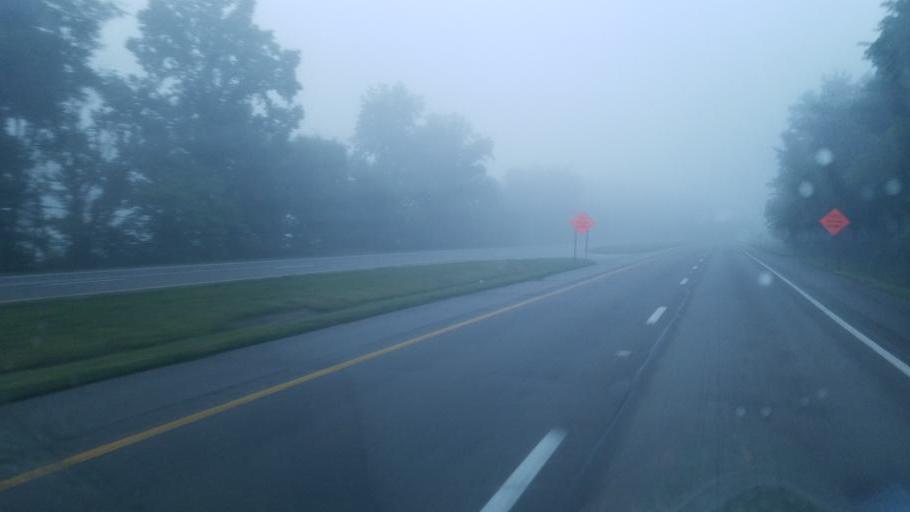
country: US
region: Ohio
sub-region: Jackson County
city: Jackson
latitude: 39.1325
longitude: -82.7090
